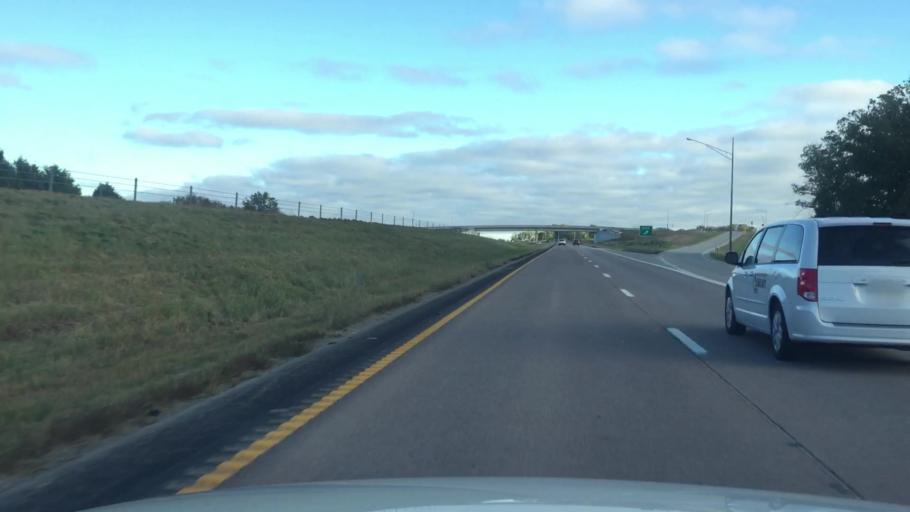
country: US
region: Missouri
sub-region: Boone County
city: Ashland
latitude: 38.8288
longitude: -92.2499
